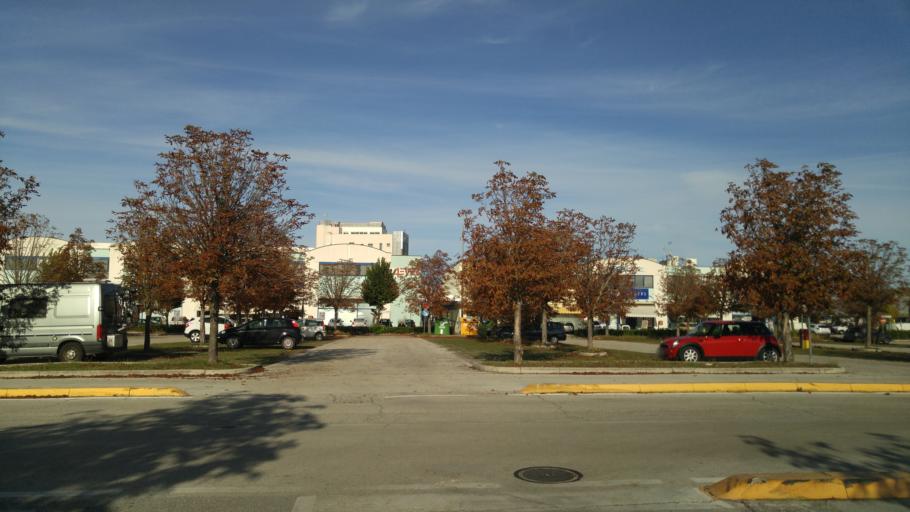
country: IT
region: The Marches
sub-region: Provincia di Pesaro e Urbino
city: Bellocchi
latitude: 43.8013
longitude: 13.0133
